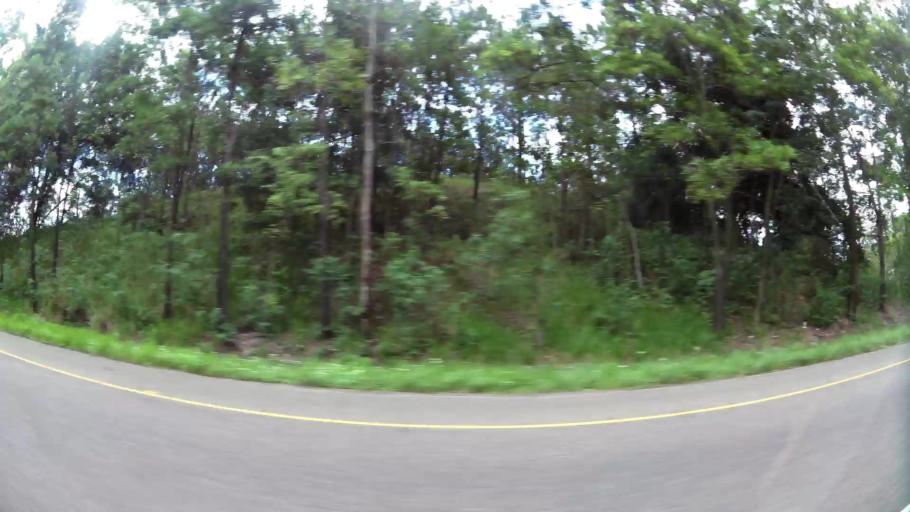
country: DO
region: La Vega
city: Rincon
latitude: 19.1093
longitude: -70.4451
